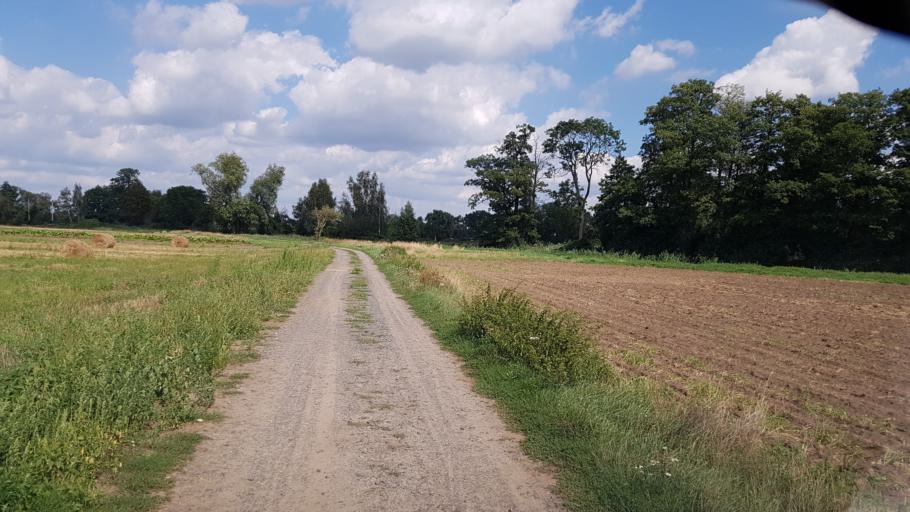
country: DE
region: Brandenburg
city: Lubbenau
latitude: 51.8699
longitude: 13.9288
